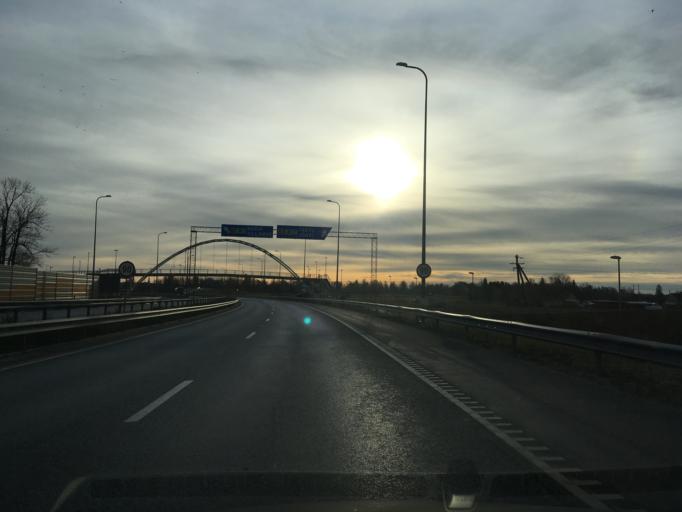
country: EE
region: Ida-Virumaa
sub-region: Johvi vald
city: Johvi
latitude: 59.3712
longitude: 27.3839
